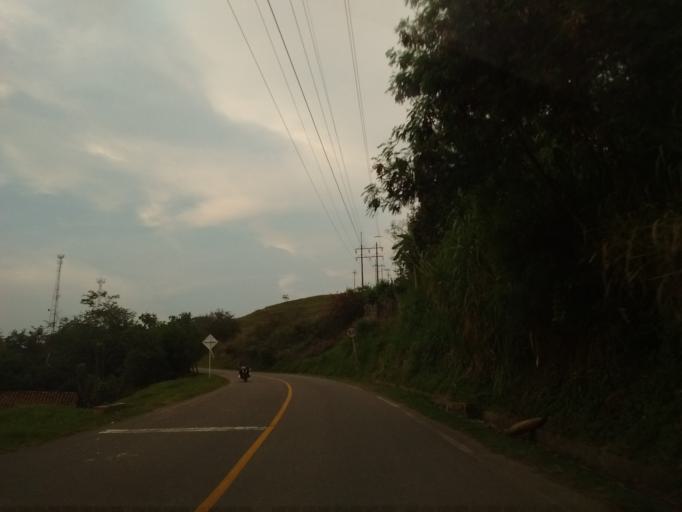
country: CO
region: Cauca
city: Caloto
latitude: 3.0668
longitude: -76.3534
